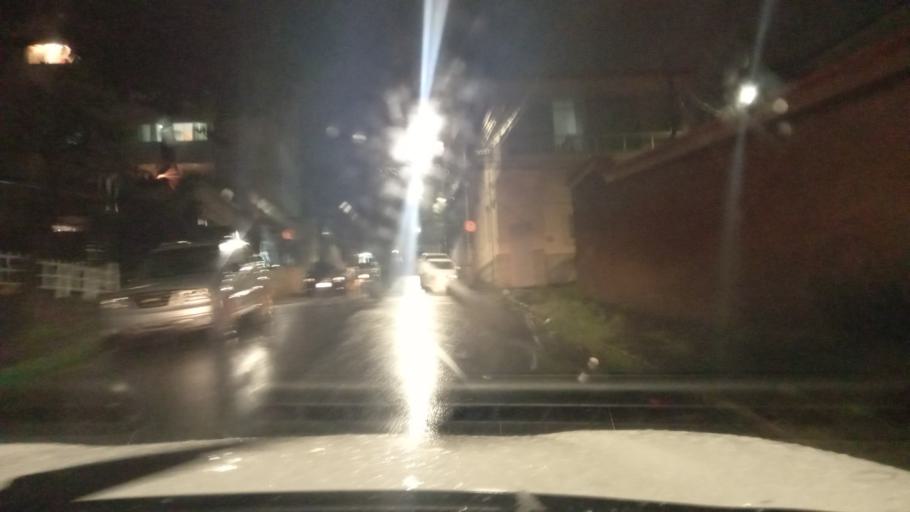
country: BR
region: Minas Gerais
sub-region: Belo Horizonte
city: Belo Horizonte
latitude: -19.9137
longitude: -43.9695
